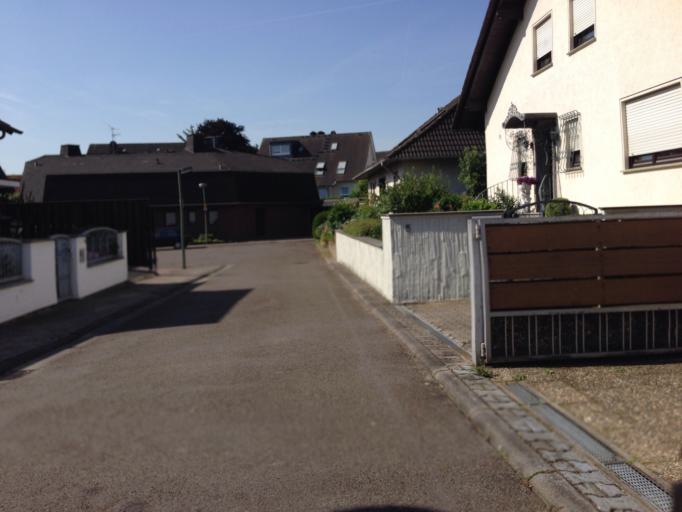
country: DE
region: Hesse
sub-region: Regierungsbezirk Darmstadt
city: Hanau am Main
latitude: 50.1149
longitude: 8.9001
